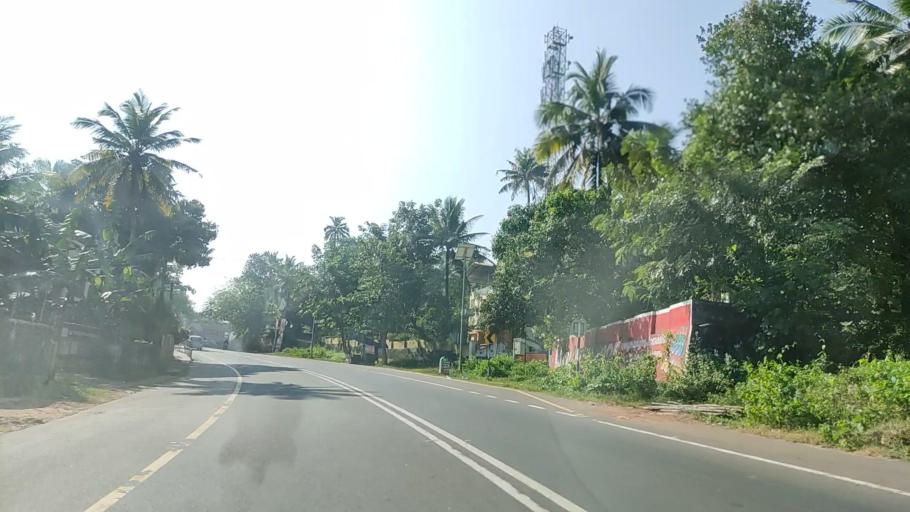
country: IN
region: Kerala
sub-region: Kollam
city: Punalur
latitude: 8.8666
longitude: 76.8702
